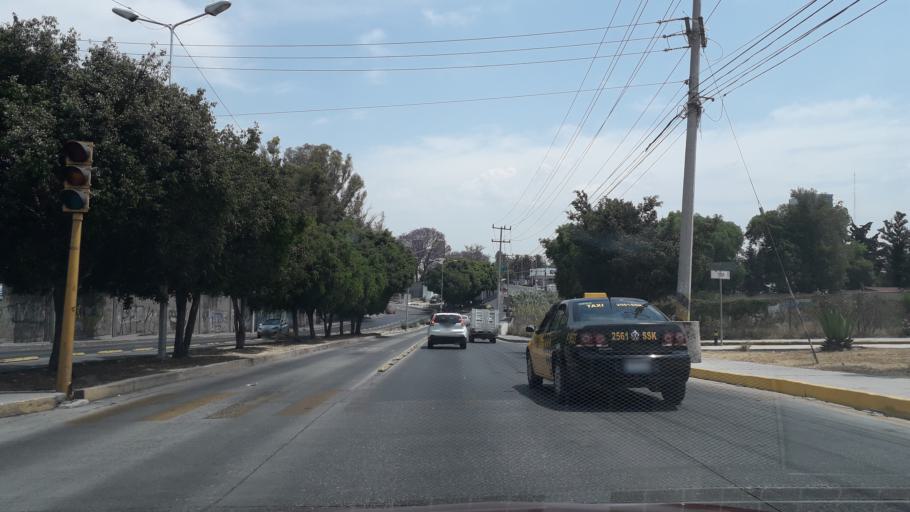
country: MX
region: Puebla
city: Puebla
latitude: 19.0178
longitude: -98.2302
